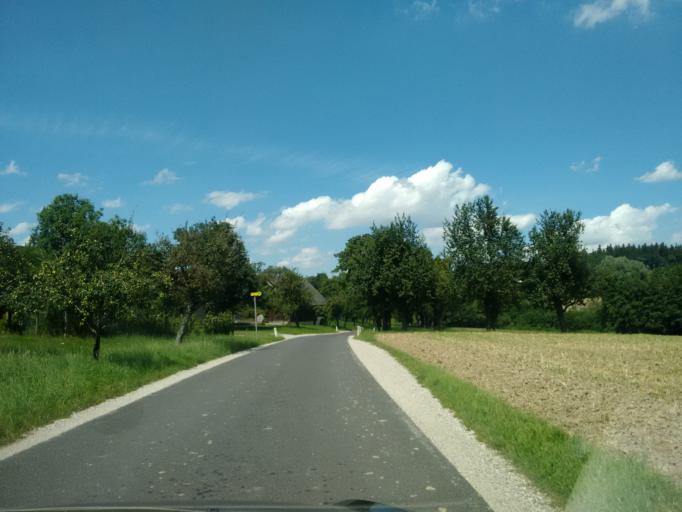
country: AT
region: Upper Austria
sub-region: Wels-Land
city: Gunskirchen
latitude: 48.1775
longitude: 13.9696
